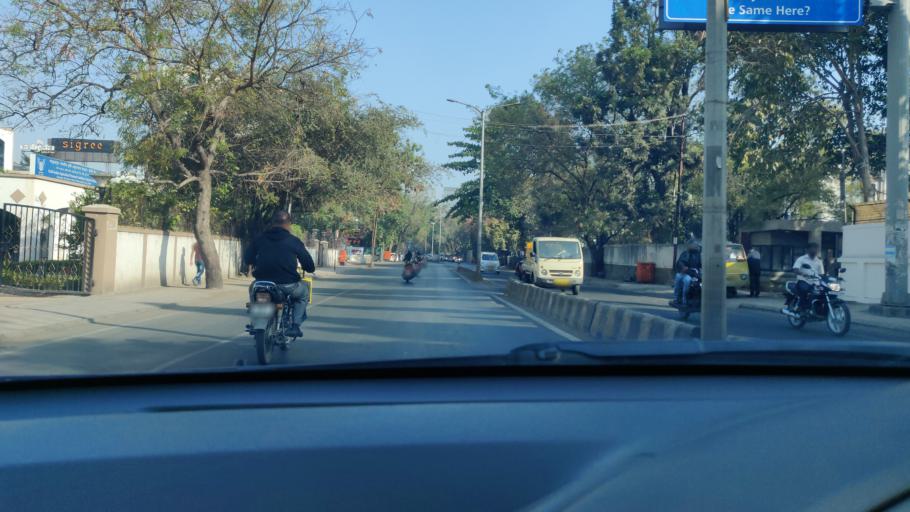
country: IN
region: Maharashtra
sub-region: Pune Division
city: Khadki
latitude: 18.5515
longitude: 73.8096
